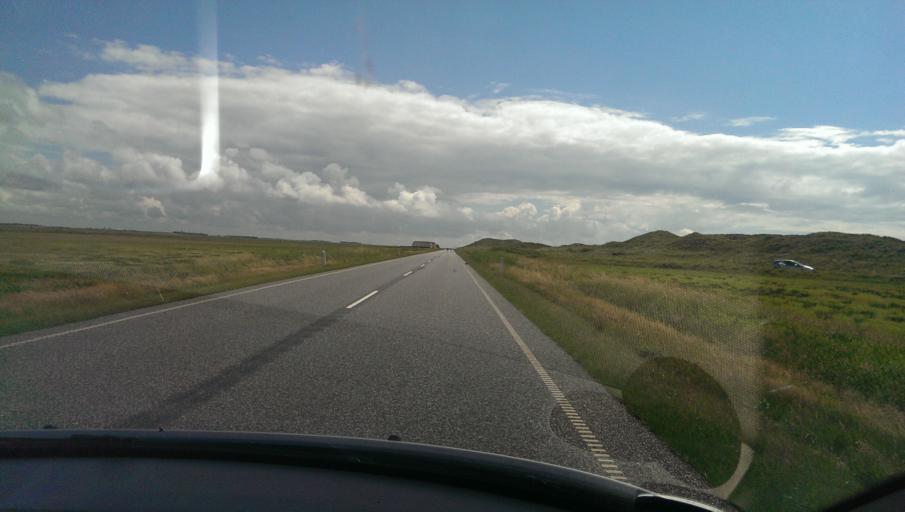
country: DK
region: Central Jutland
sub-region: Ringkobing-Skjern Kommune
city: Ringkobing
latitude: 56.2374
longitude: 8.1386
